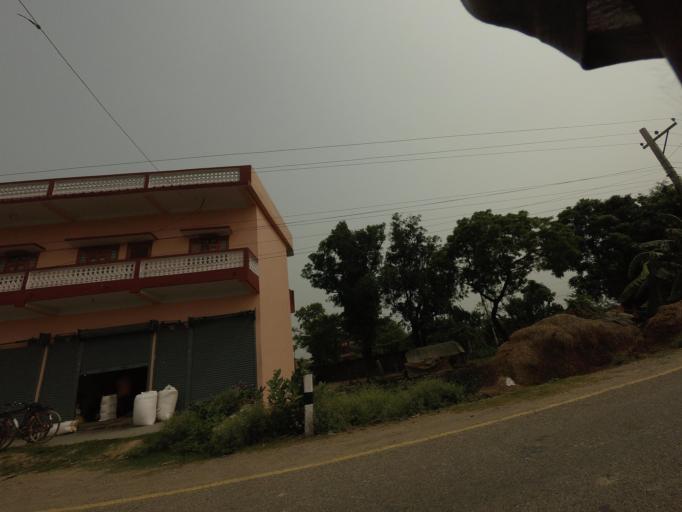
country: NP
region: Western Region
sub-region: Lumbini Zone
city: Bhairahawa
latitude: 27.5045
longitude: 83.3471
